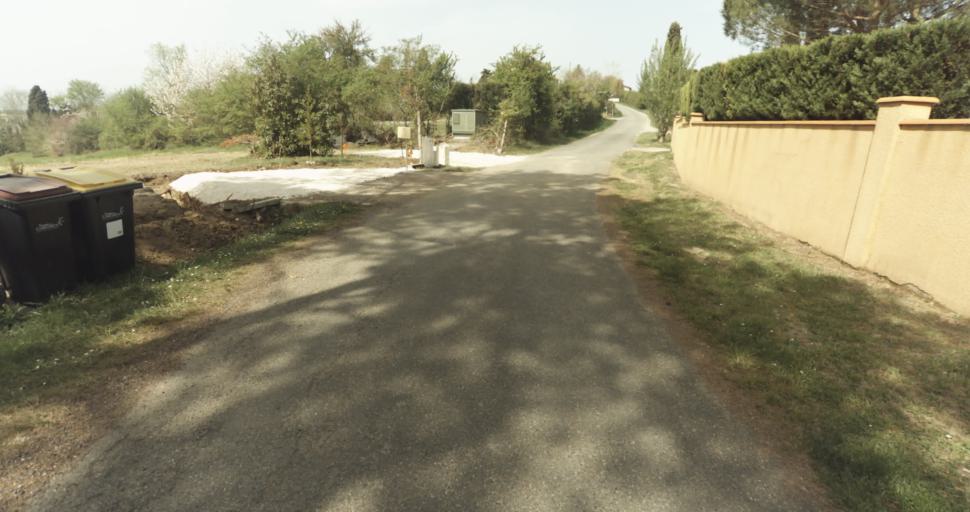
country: FR
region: Midi-Pyrenees
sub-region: Departement du Tarn-et-Garonne
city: Moissac
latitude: 44.1054
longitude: 1.0799
